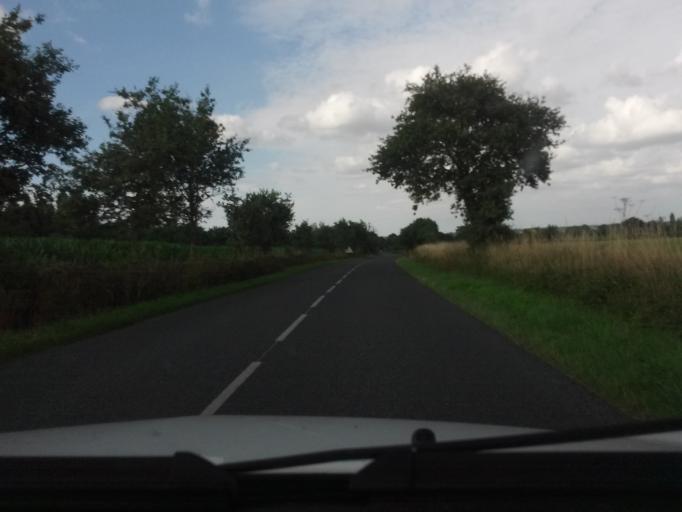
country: FR
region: Pays de la Loire
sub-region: Departement de la Vendee
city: La Bruffiere
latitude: 47.0028
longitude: -1.2101
